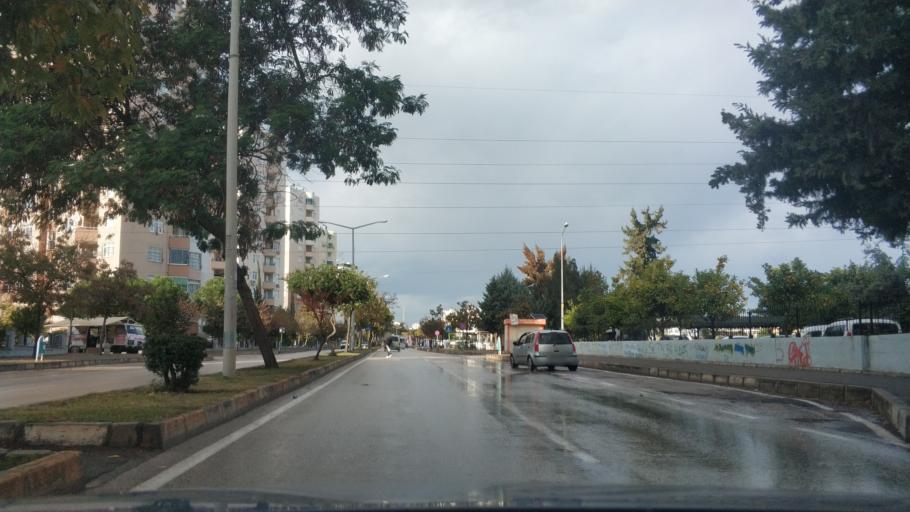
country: TR
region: Adana
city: Seyhan
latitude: 37.0381
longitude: 35.2614
